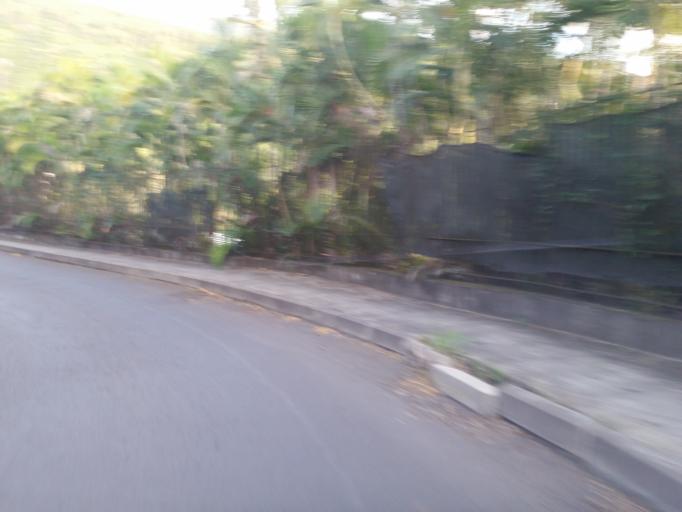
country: RE
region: Reunion
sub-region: Reunion
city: Saint-Denis
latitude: -20.9011
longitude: 55.4574
